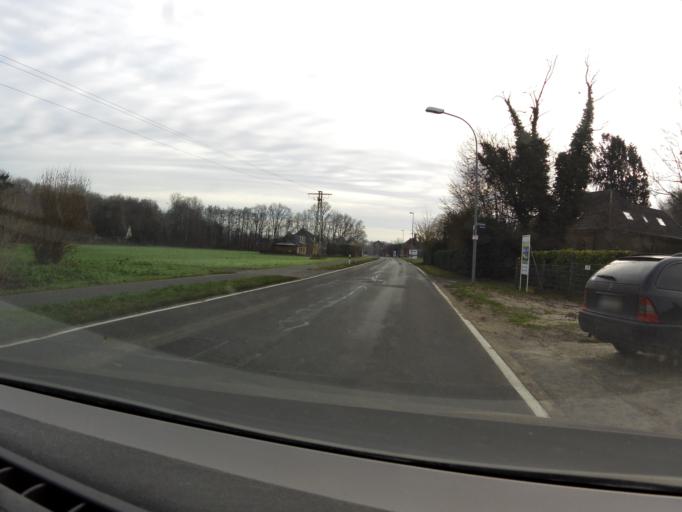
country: DE
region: North Rhine-Westphalia
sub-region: Regierungsbezirk Dusseldorf
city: Nettetal
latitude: 51.3082
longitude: 6.2425
